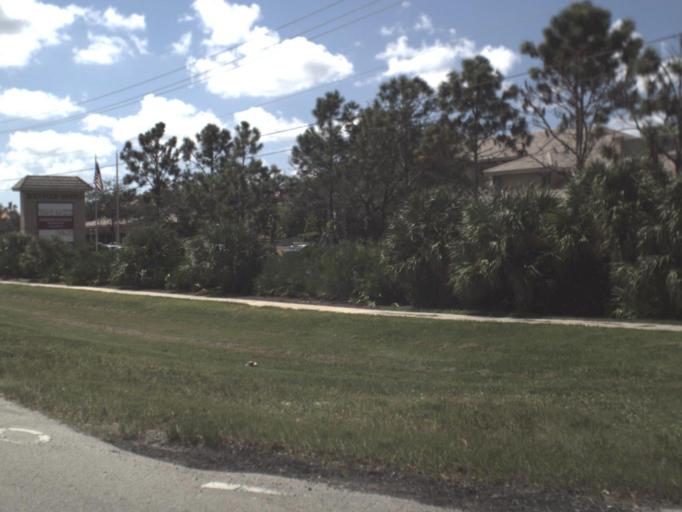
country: US
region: Florida
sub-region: Lee County
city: Bonita Springs
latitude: 26.3779
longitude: -81.8080
